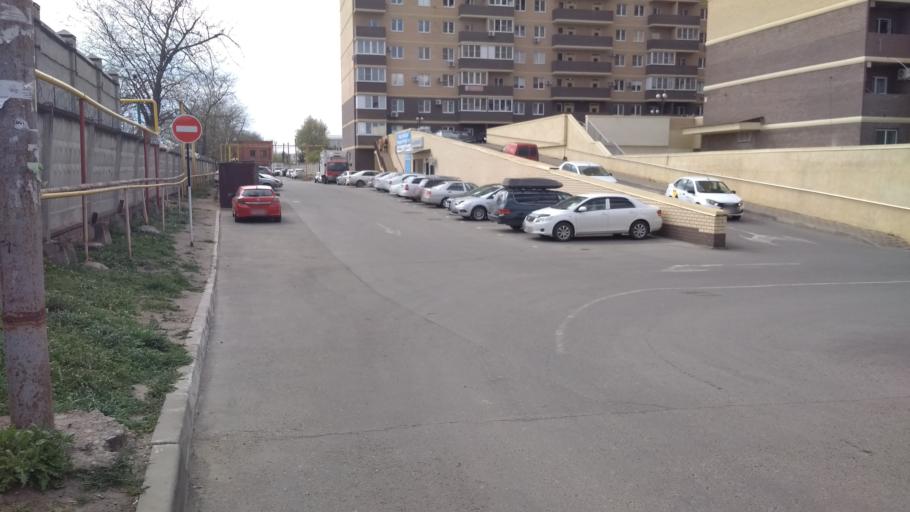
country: RU
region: Krasnodarskiy
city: Krasnodar
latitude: 45.0771
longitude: 39.0046
